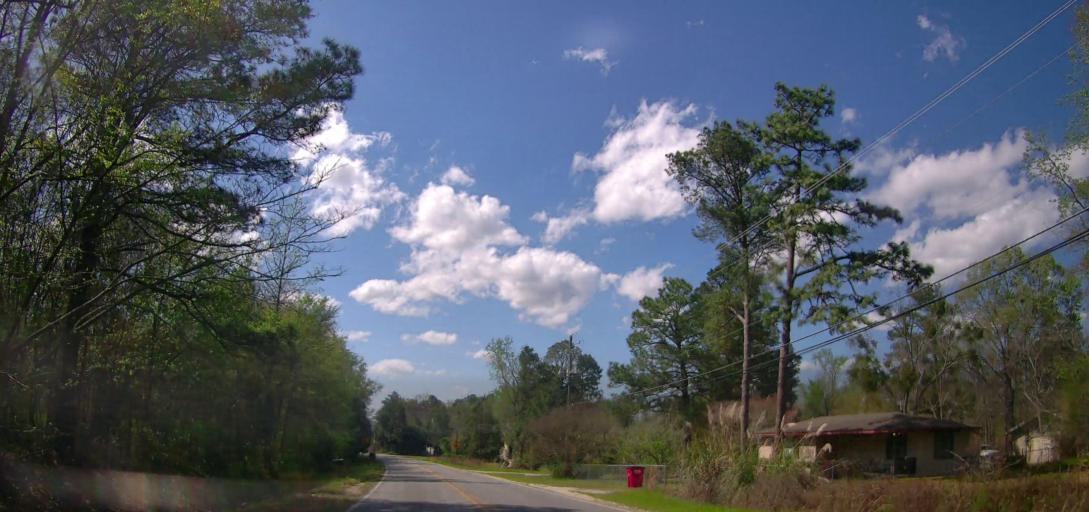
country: US
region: Georgia
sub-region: Bibb County
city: Macon
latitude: 32.8373
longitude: -83.5716
